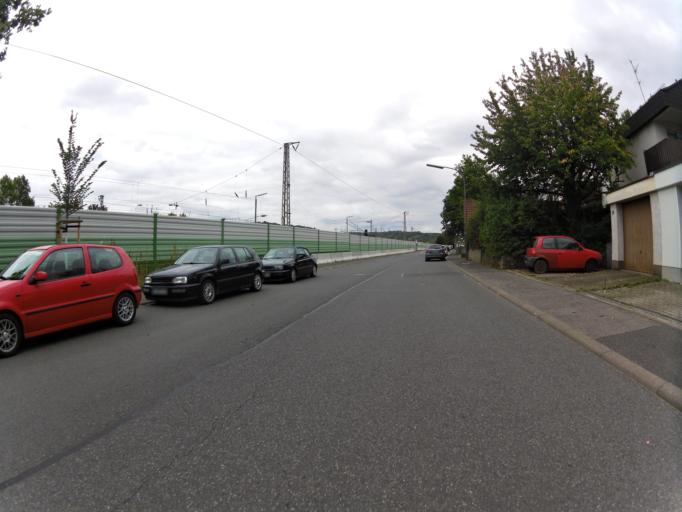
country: DE
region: Bavaria
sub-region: Regierungsbezirk Unterfranken
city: Randersacker
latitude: 49.7604
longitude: 9.9575
